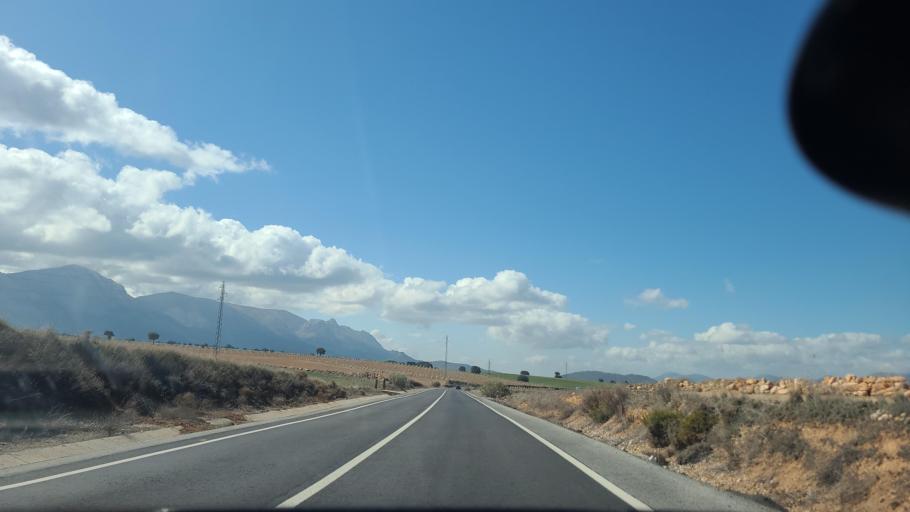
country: ES
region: Andalusia
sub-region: Provincia de Granada
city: Pinar
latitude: 37.3990
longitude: -3.4159
